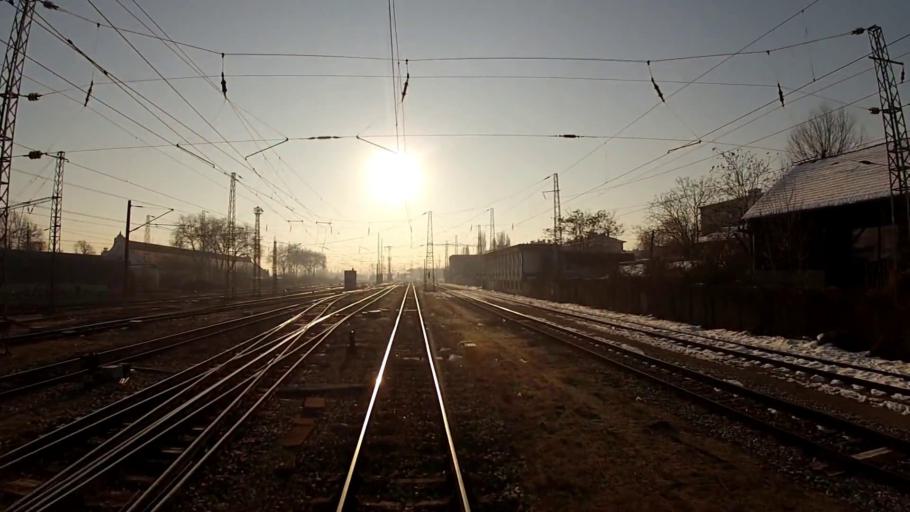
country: BG
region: Sofia-Capital
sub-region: Stolichna Obshtina
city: Sofia
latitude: 42.7230
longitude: 23.2946
